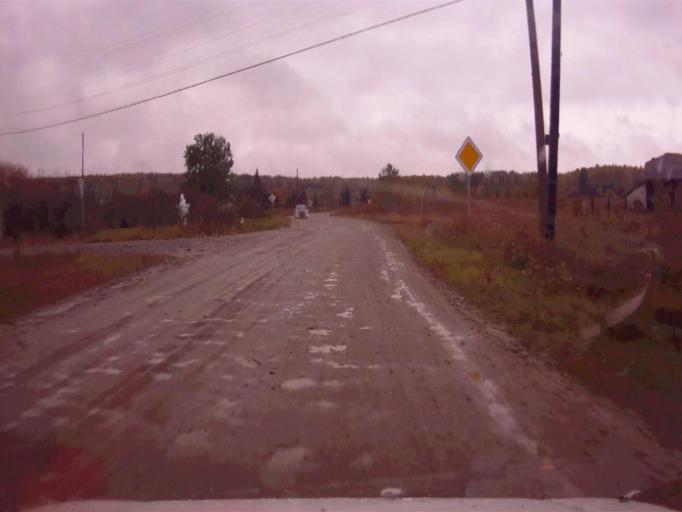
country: RU
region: Chelyabinsk
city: Kyshtym
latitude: 55.8521
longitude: 60.4825
